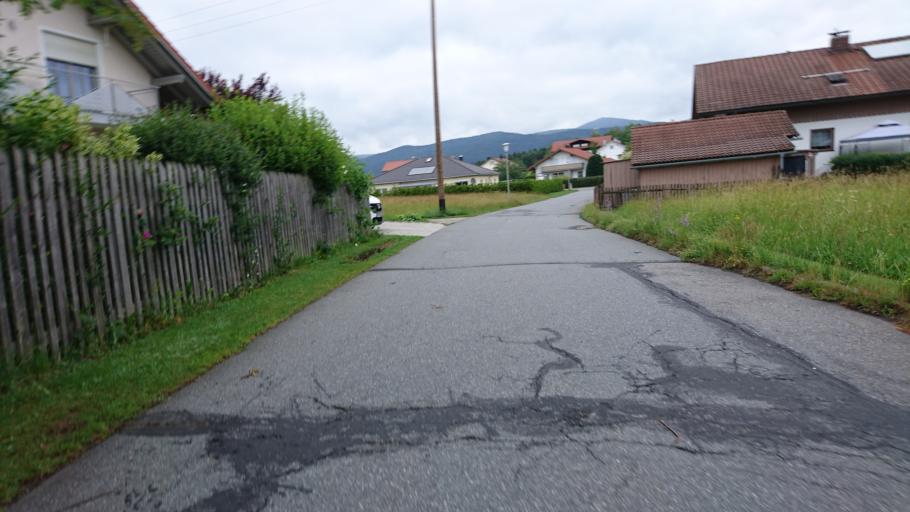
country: DE
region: Bavaria
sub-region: Lower Bavaria
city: Neuschonau
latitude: 48.8829
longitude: 13.4697
